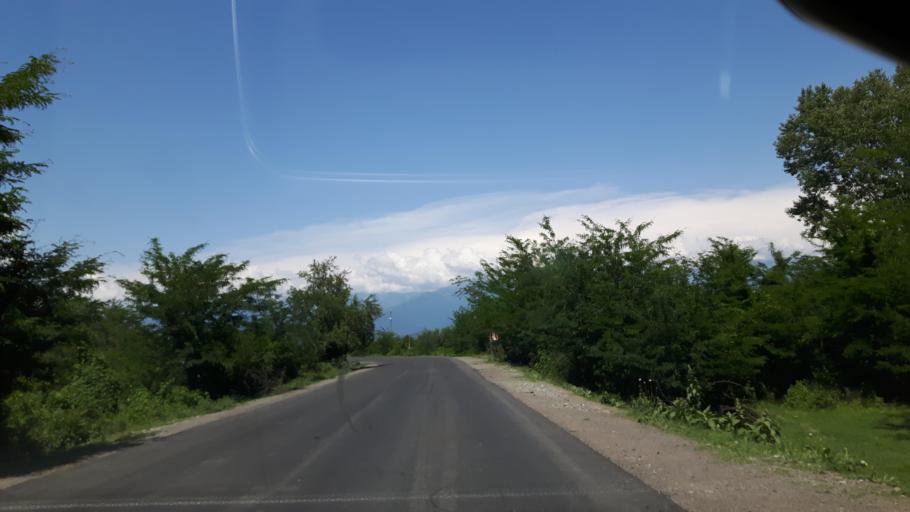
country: GE
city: Bagdadi
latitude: 41.7051
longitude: 46.0860
